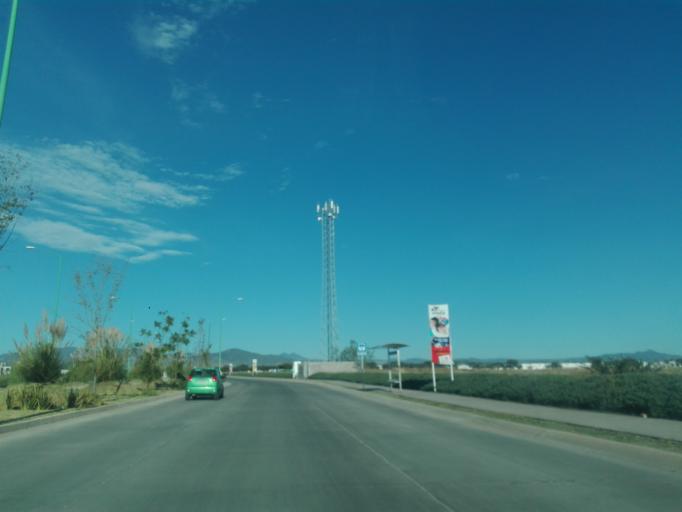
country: MX
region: Guanajuato
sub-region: Leon
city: Ladrilleras del Refugio
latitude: 21.0631
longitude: -101.5726
